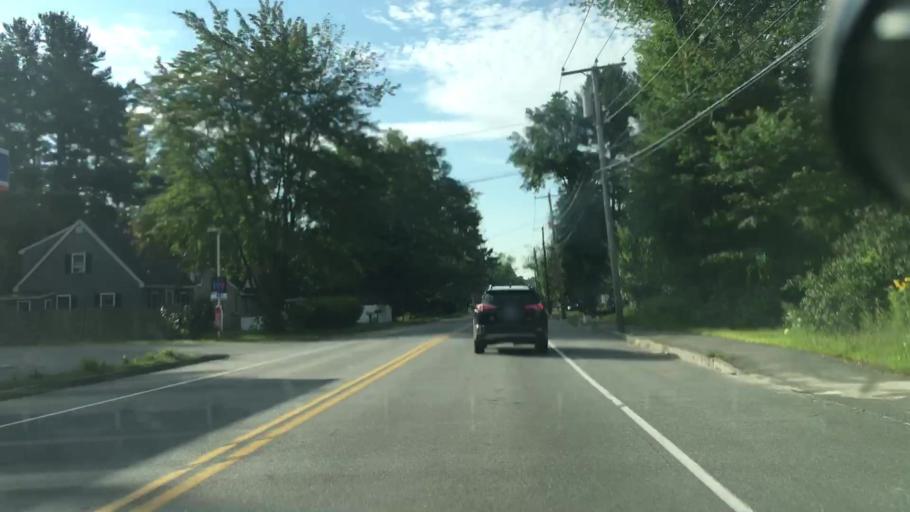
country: US
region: Maine
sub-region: Cumberland County
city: Westbrook
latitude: 43.7086
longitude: -70.3290
